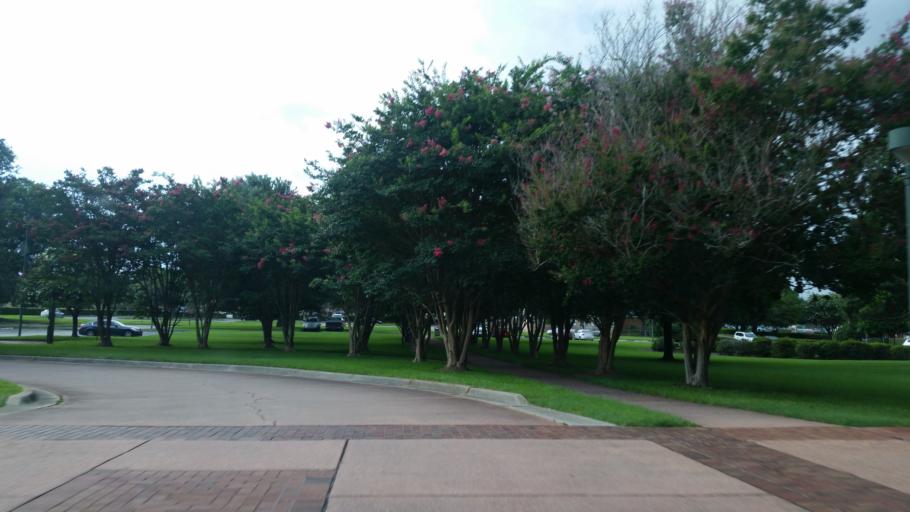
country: US
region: Florida
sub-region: Escambia County
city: Pensacola
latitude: 30.4147
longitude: -87.2028
